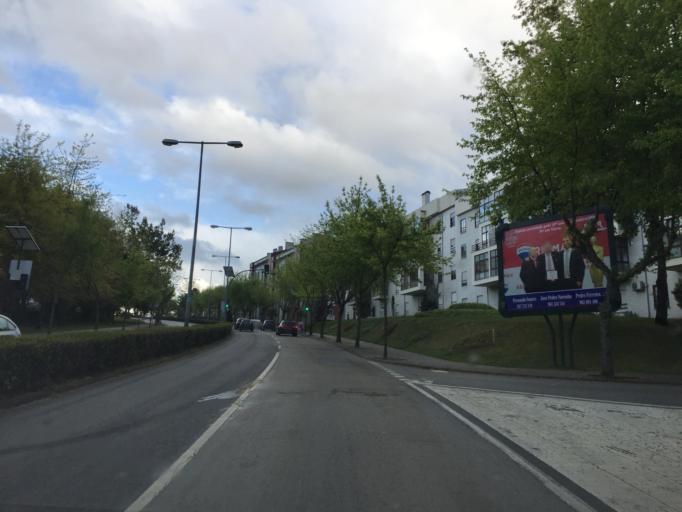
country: PT
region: Viseu
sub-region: Viseu
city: Viseu
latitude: 40.6518
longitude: -7.9215
